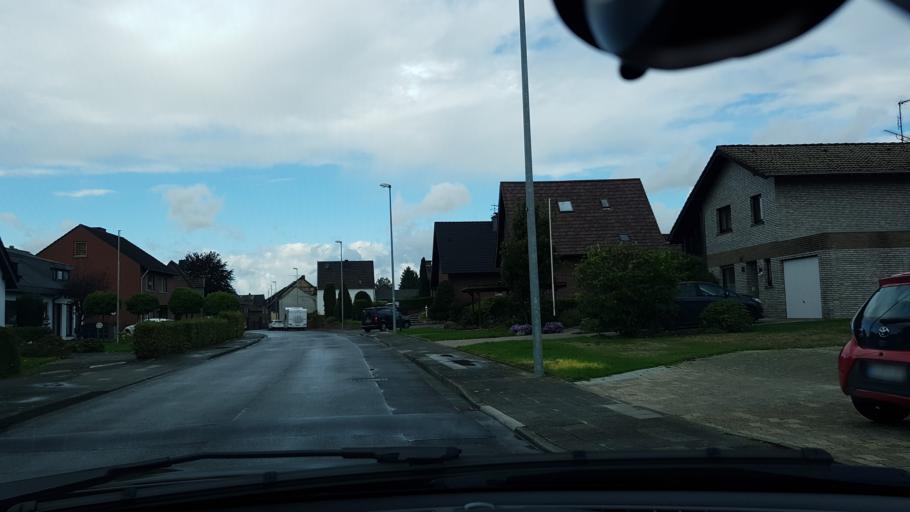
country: DE
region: North Rhine-Westphalia
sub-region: Regierungsbezirk Koln
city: Wassenberg
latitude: 51.0850
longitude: 6.1534
